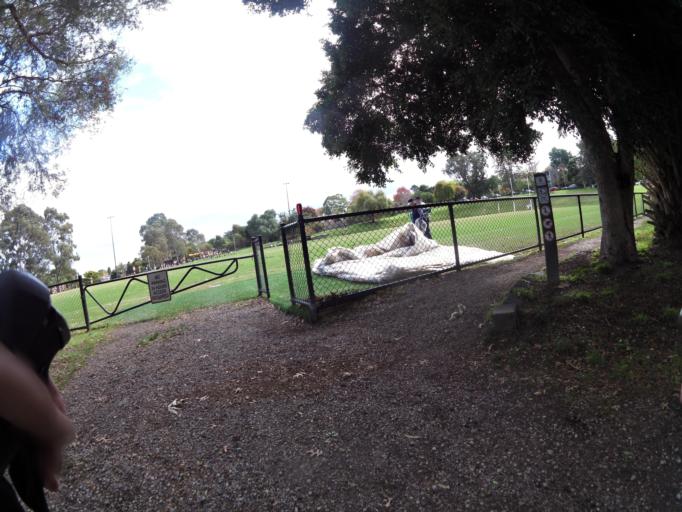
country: AU
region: Victoria
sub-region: Boroondara
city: Hawthorn East
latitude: -37.8199
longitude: 145.0549
